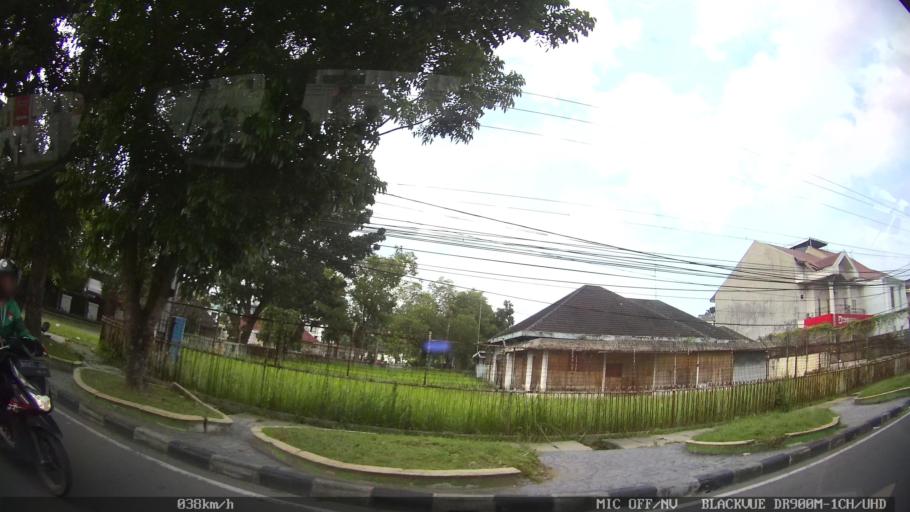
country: ID
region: North Sumatra
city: Medan
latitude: 3.5723
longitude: 98.6736
